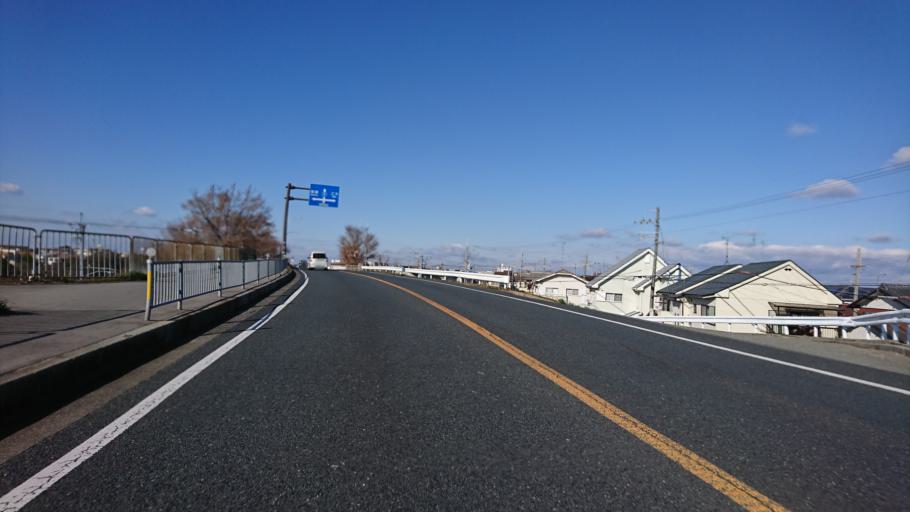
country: JP
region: Hyogo
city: Kakogawacho-honmachi
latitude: 34.7277
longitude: 134.8854
